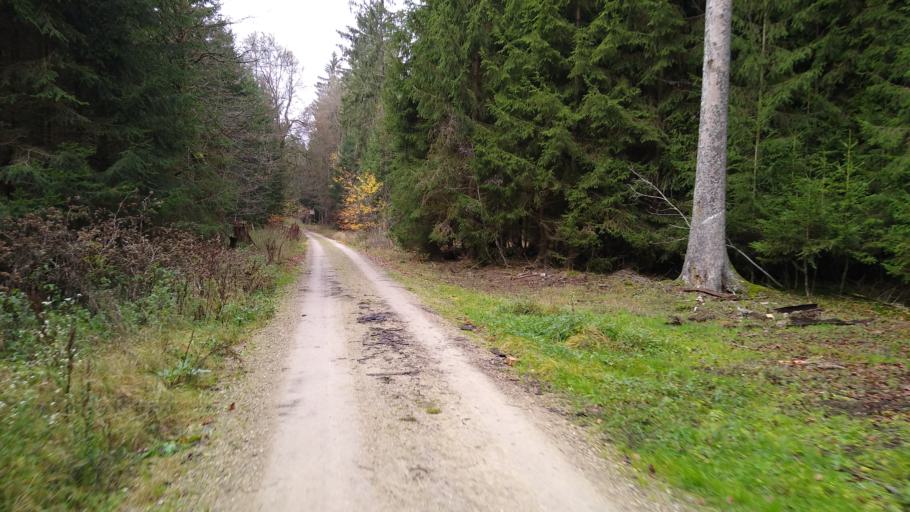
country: DE
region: Bavaria
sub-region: Upper Palatinate
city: Seubersdorf
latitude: 49.1438
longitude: 11.6332
